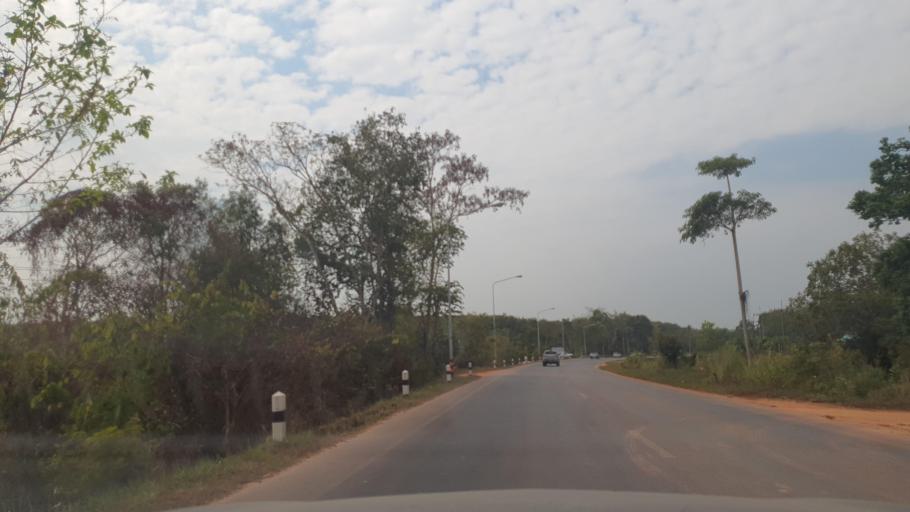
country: TH
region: Changwat Bueng Kan
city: Si Wilai
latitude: 18.2721
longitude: 103.8406
